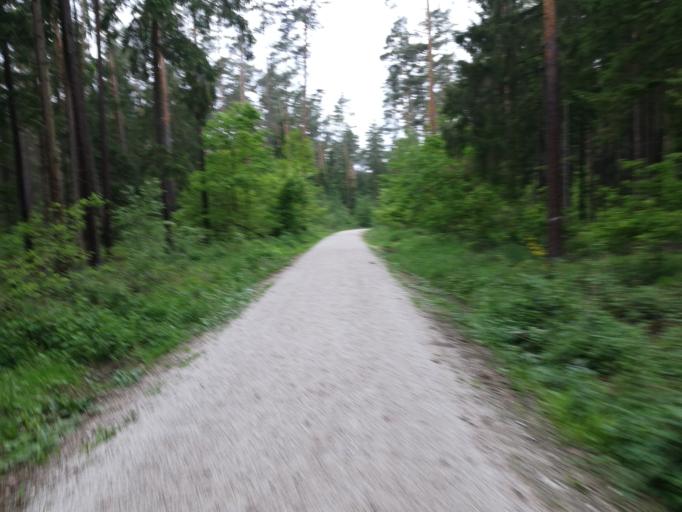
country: DE
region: Bavaria
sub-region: Regierungsbezirk Mittelfranken
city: Seukendorf
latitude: 49.4652
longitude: 10.8971
